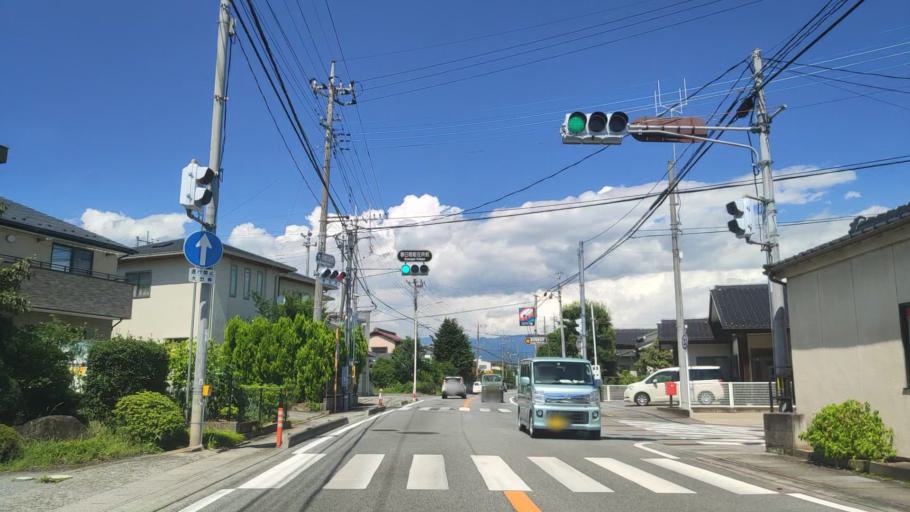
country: JP
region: Yamanashi
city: Isawa
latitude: 35.6697
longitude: 138.6492
